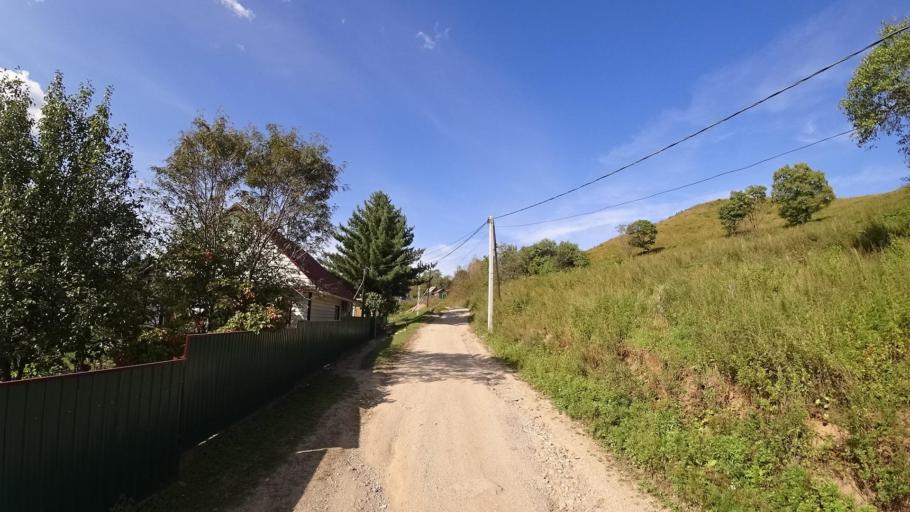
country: RU
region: Jewish Autonomous Oblast
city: Birakan
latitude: 48.9998
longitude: 131.7214
